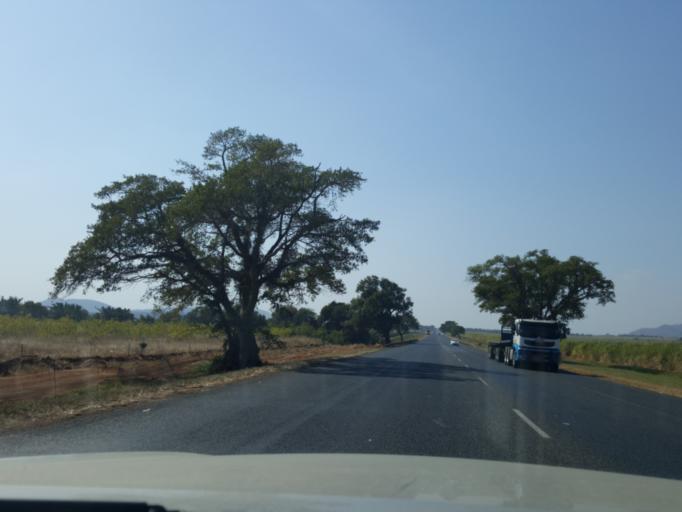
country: SZ
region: Hhohho
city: Ntfonjeni
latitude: -25.4910
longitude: 31.5276
